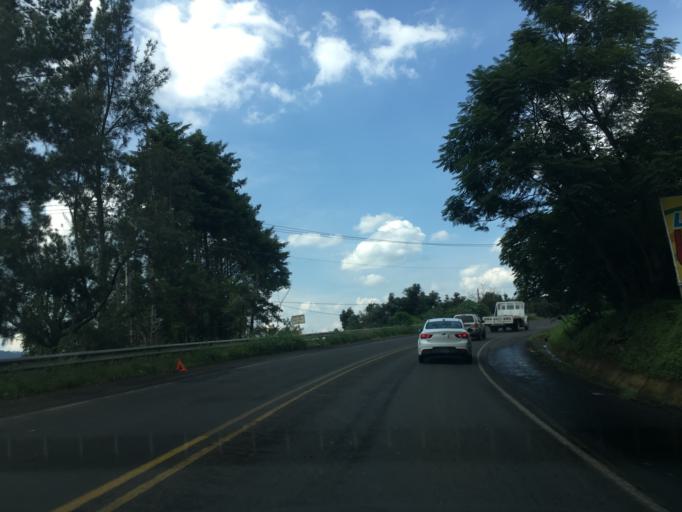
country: MX
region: Michoacan
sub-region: Tingueindin
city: Tingueindin
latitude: 19.7447
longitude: -102.4859
